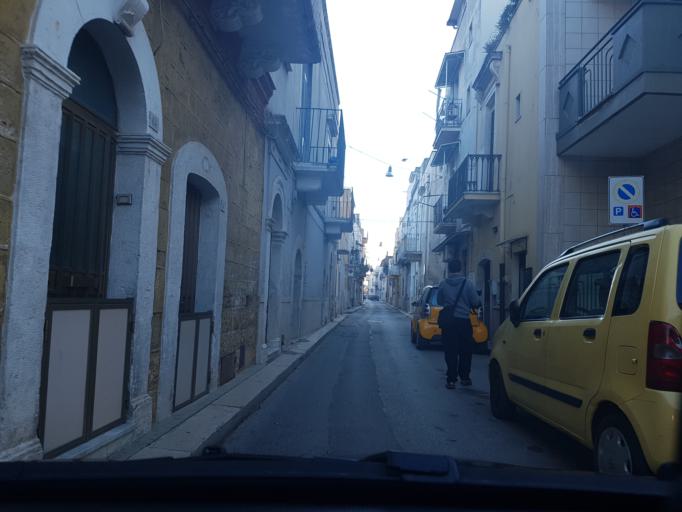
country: IT
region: Apulia
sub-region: Provincia di Bari
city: Bitritto
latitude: 41.0399
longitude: 16.8265
